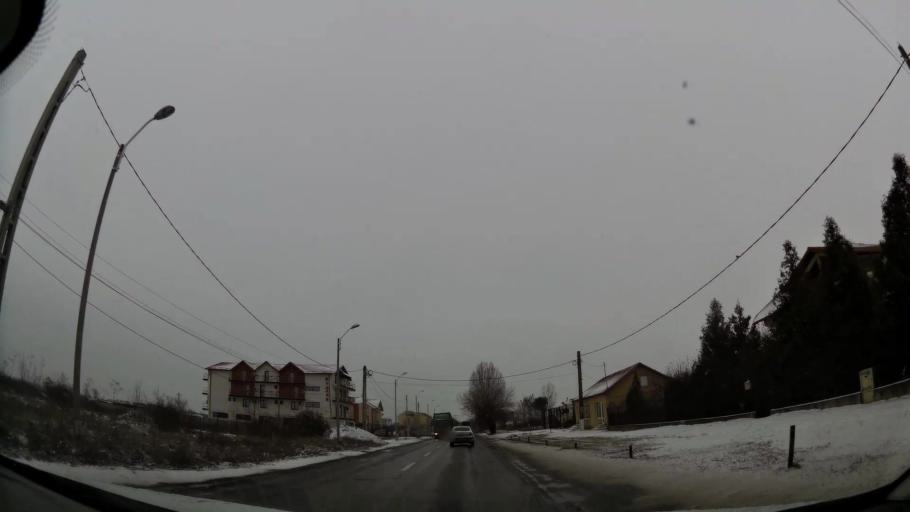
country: RO
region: Dambovita
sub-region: Comuna Ulmi
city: Ulmi
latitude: 44.9022
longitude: 25.4990
